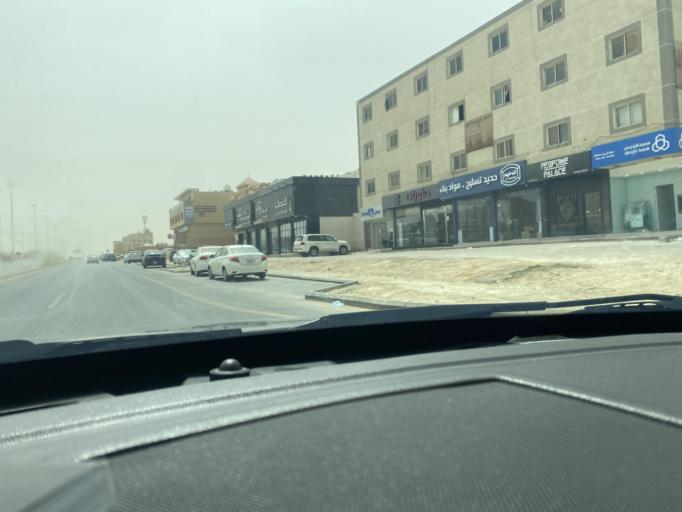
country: SA
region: Ar Riyad
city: Riyadh
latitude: 24.8179
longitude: 46.5929
